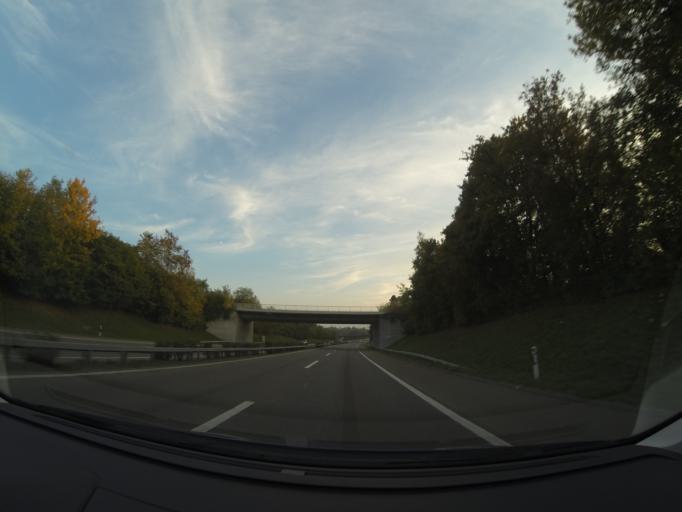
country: CH
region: Zurich
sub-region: Bezirk Hinwil
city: Durnten
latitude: 47.2689
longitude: 8.8321
